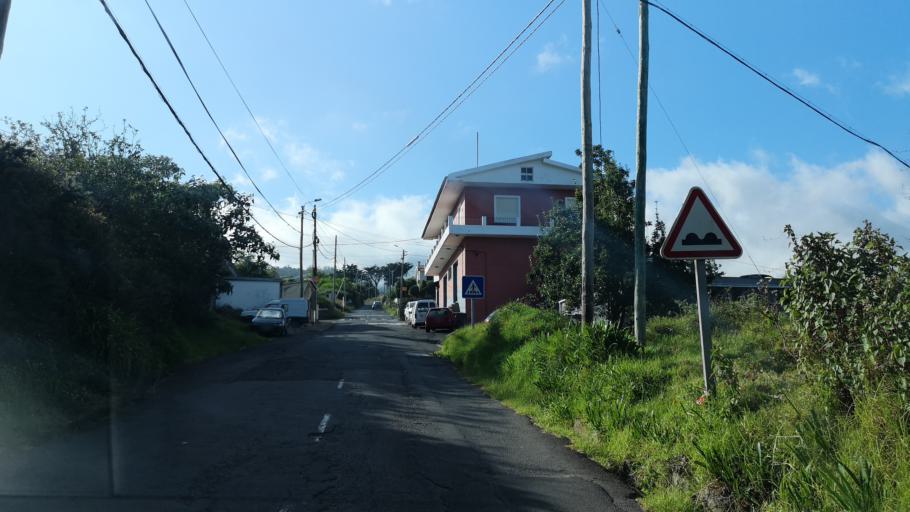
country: PT
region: Madeira
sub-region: Santa Cruz
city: Camacha
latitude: 32.6681
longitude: -16.8421
